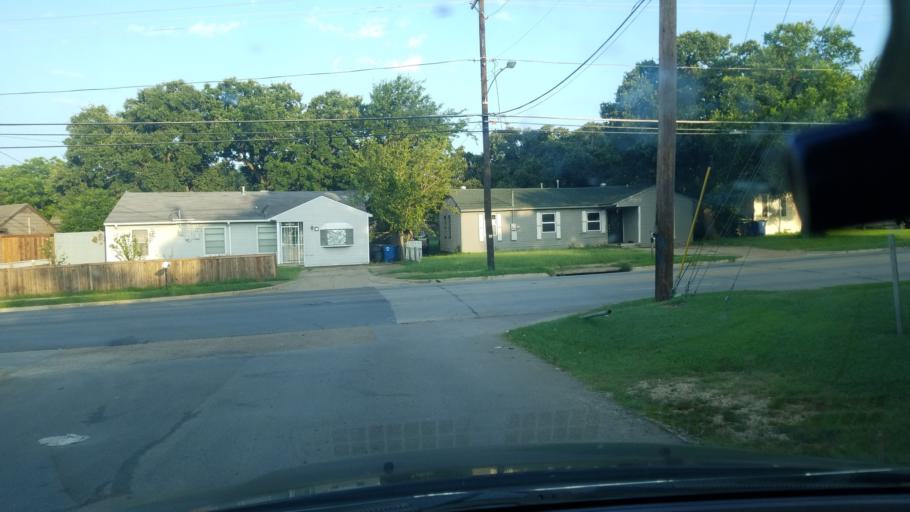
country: US
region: Texas
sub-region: Dallas County
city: Balch Springs
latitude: 32.7237
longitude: -96.6568
